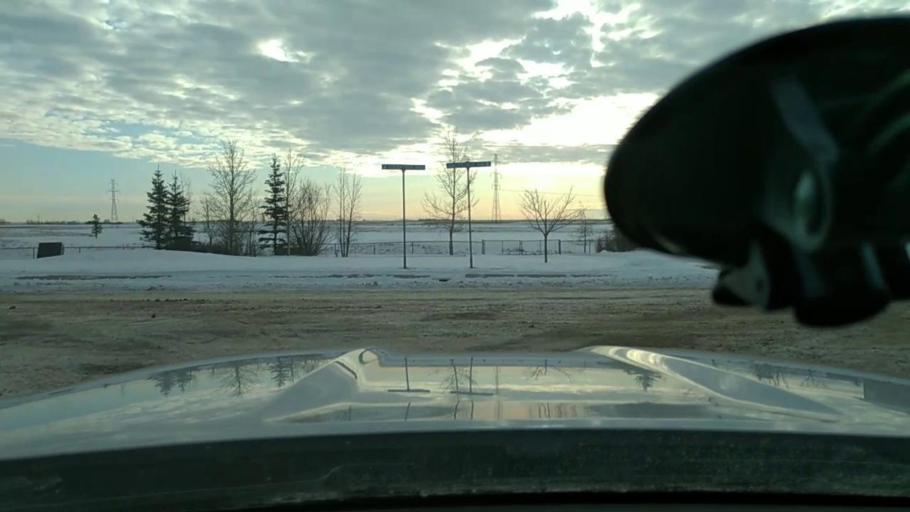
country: CA
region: Alberta
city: Chestermere
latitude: 50.9608
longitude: -113.6612
